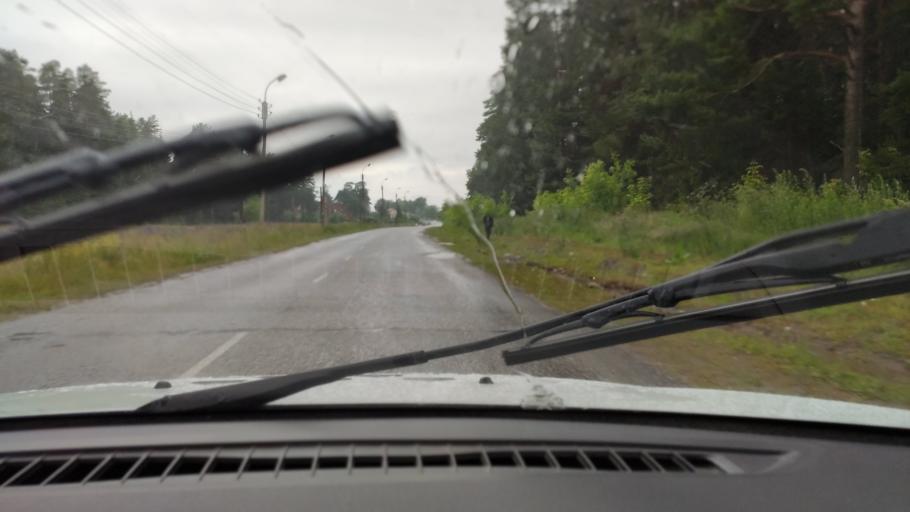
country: RU
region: Udmurtiya
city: Votkinsk
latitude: 57.0668
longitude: 54.0312
